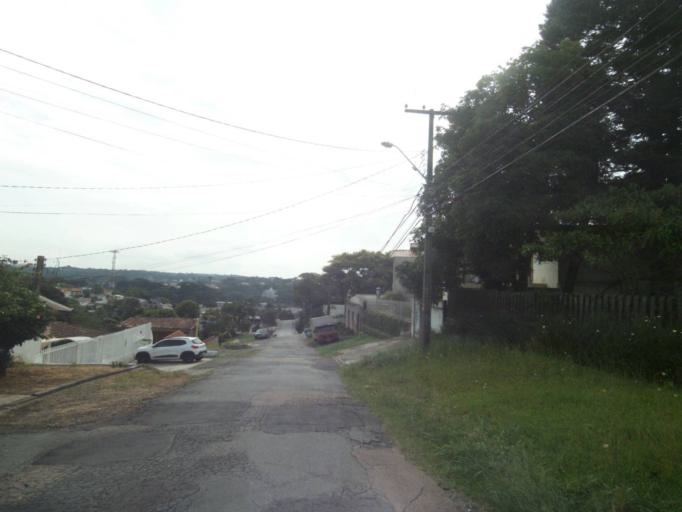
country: BR
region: Parana
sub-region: Curitiba
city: Curitiba
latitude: -25.4091
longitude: -49.2994
